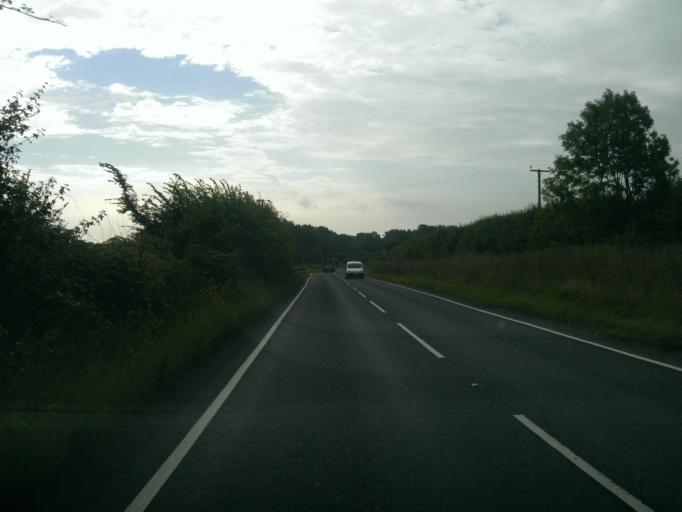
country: GB
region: England
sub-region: Essex
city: Great Bentley
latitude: 51.8360
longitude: 1.0530
